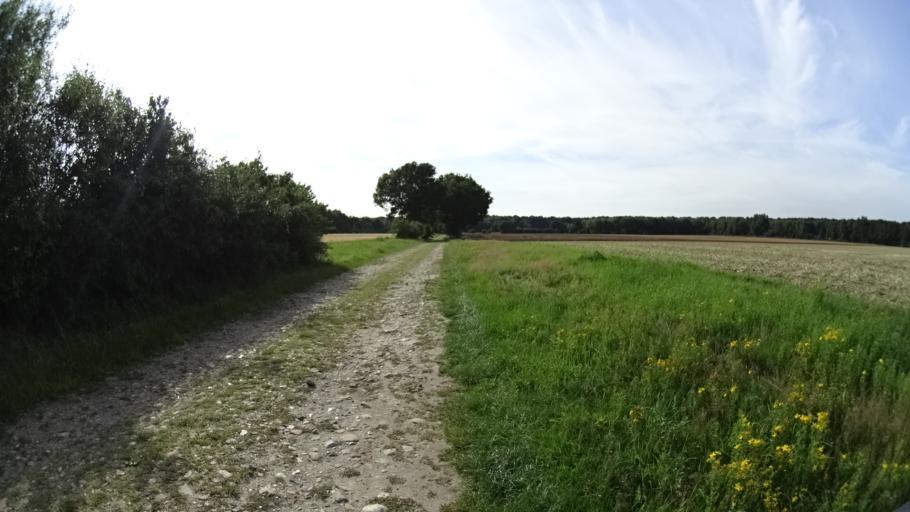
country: DE
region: Lower Saxony
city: Bardowick
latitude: 53.2789
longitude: 10.3745
